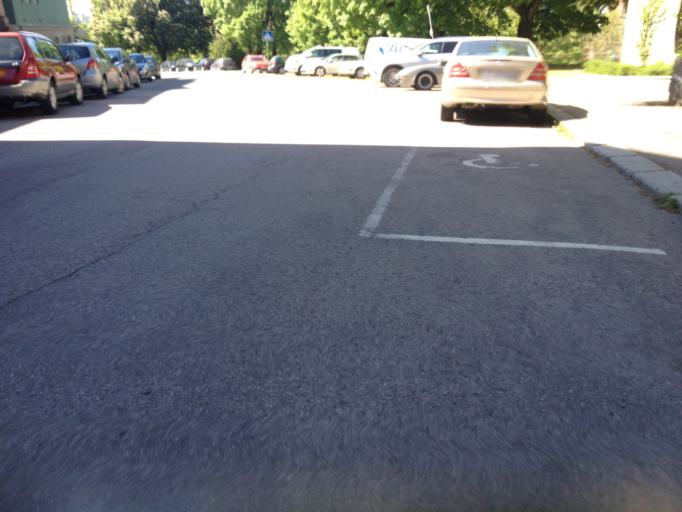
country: NO
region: Oslo
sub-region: Oslo
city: Oslo
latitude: 59.9319
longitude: 10.7599
